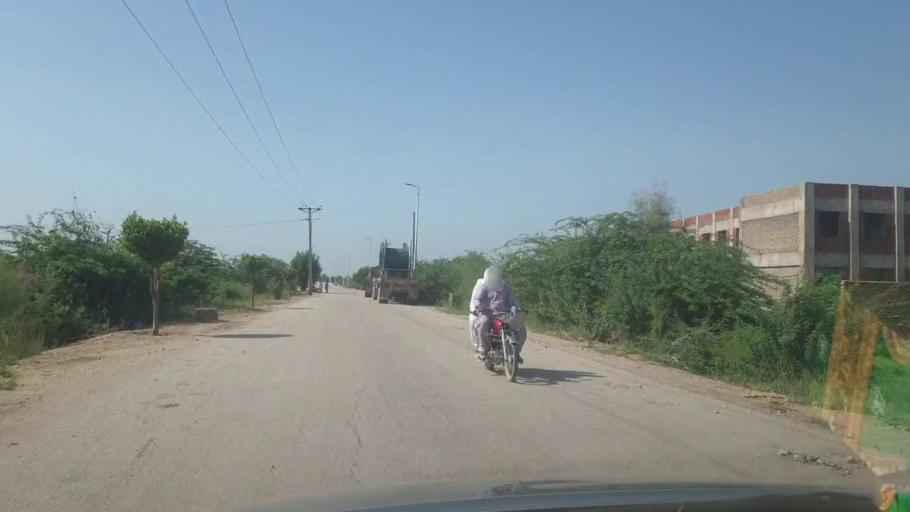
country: PK
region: Sindh
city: Rohri
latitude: 27.5158
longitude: 69.0358
